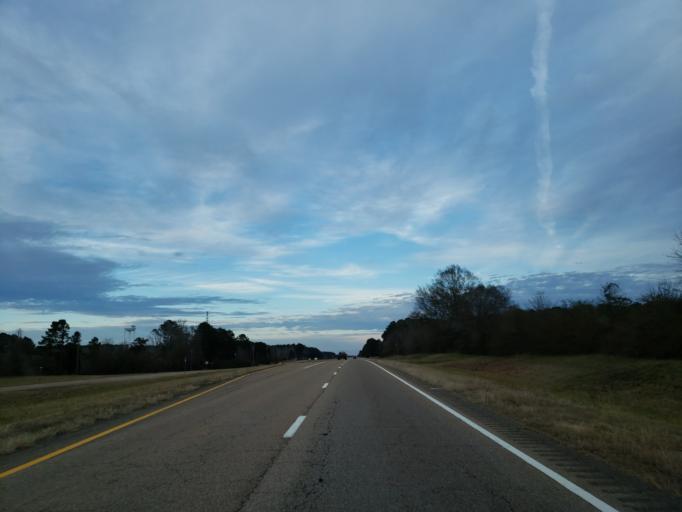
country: US
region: Mississippi
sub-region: Lauderdale County
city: Marion
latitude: 32.4711
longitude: -88.6099
